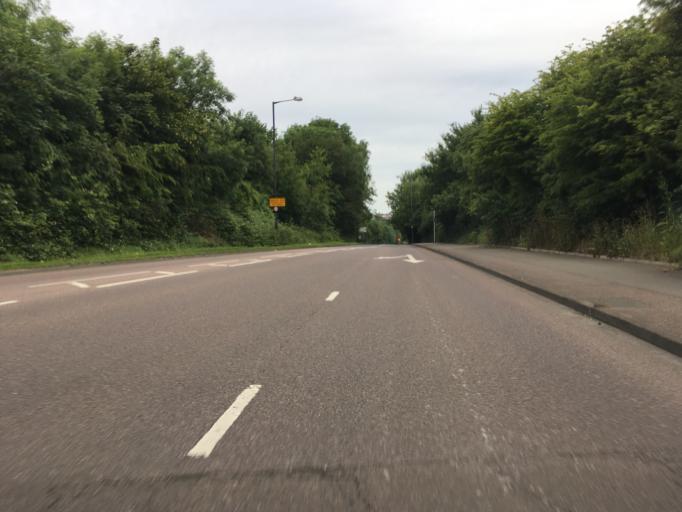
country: GB
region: England
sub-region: Bath and North East Somerset
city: Whitchurch
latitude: 51.4170
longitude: -2.5973
